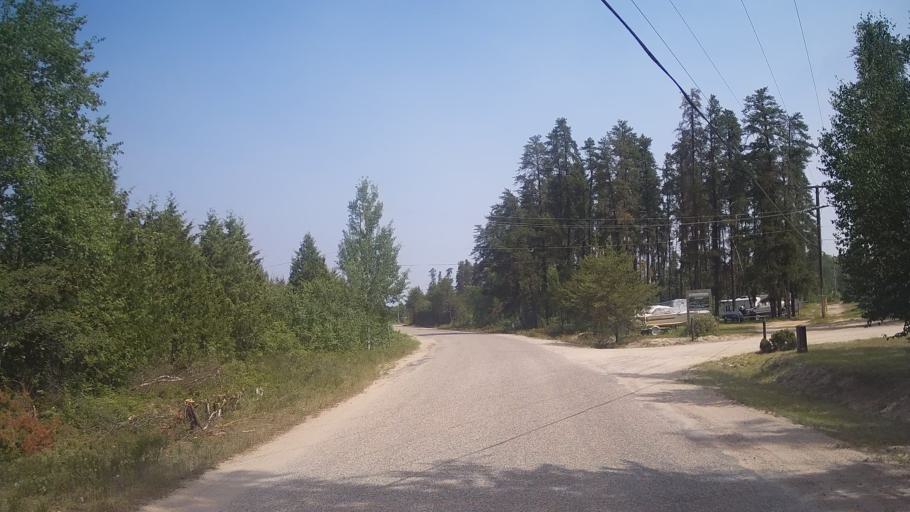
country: CA
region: Ontario
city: Timmins
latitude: 47.6824
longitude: -81.7140
